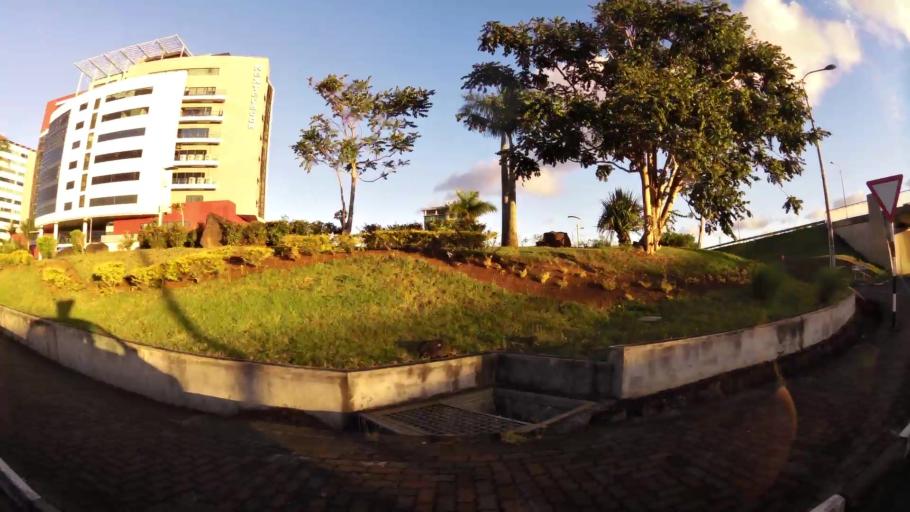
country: MU
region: Plaines Wilhems
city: Ebene
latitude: -20.2419
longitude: 57.4867
